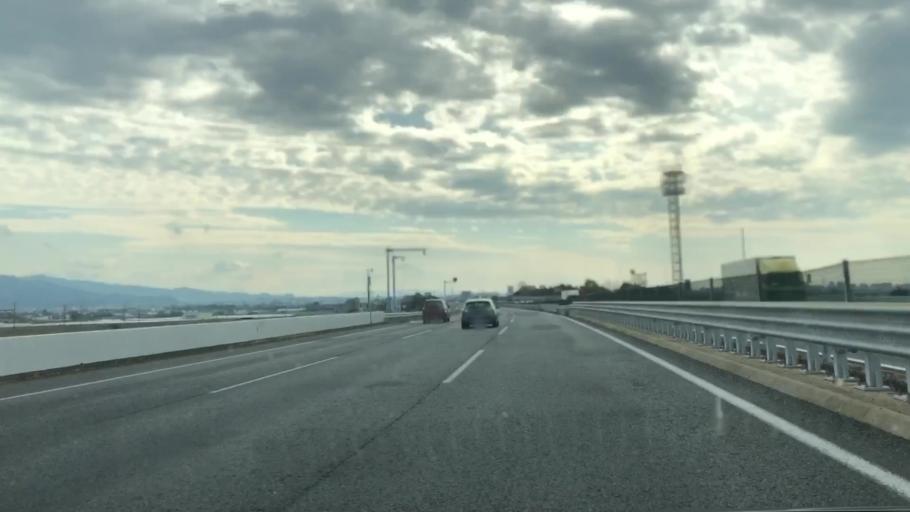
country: JP
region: Saga Prefecture
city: Tosu
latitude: 33.3534
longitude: 130.5380
